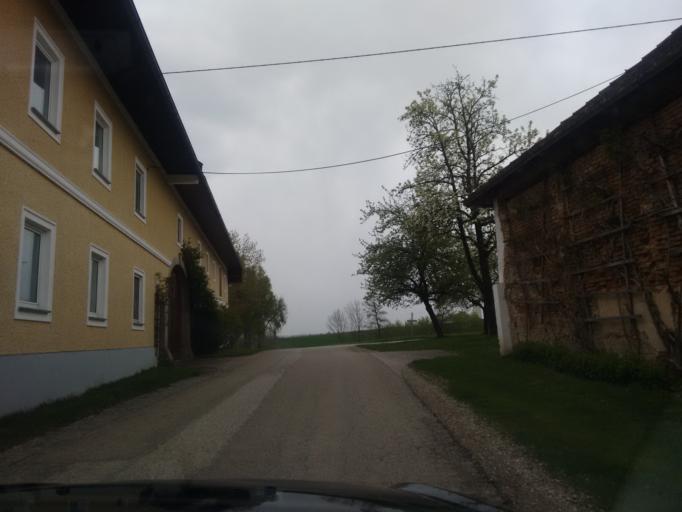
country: AT
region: Upper Austria
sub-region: Wels-Land
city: Holzhausen
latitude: 48.2144
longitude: 14.0627
